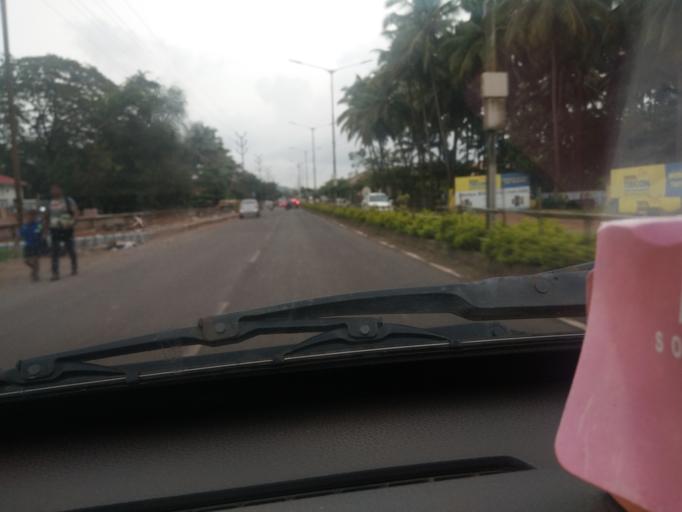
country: IN
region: Goa
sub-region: South Goa
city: Madgaon
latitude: 15.2847
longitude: 73.9602
